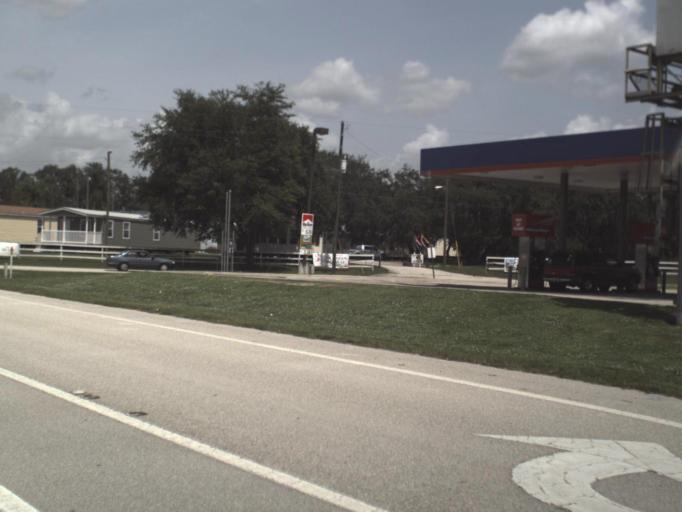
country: US
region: Florida
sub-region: Highlands County
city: Sebring
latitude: 27.4523
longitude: -81.4208
